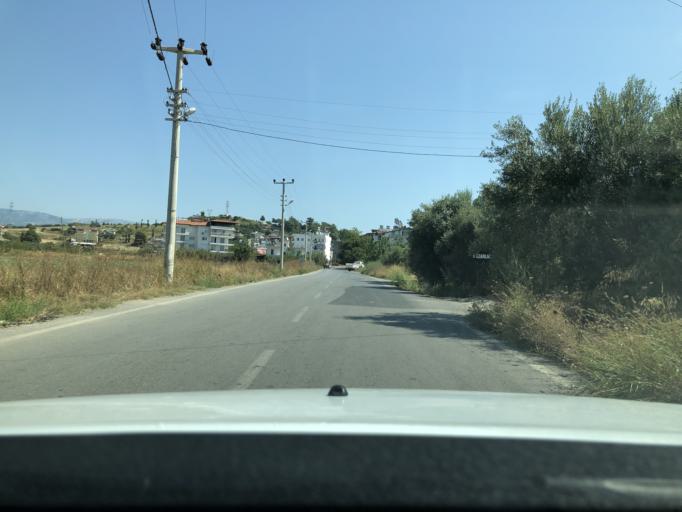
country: TR
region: Antalya
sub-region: Manavgat
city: Manavgat
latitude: 36.8083
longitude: 31.4811
